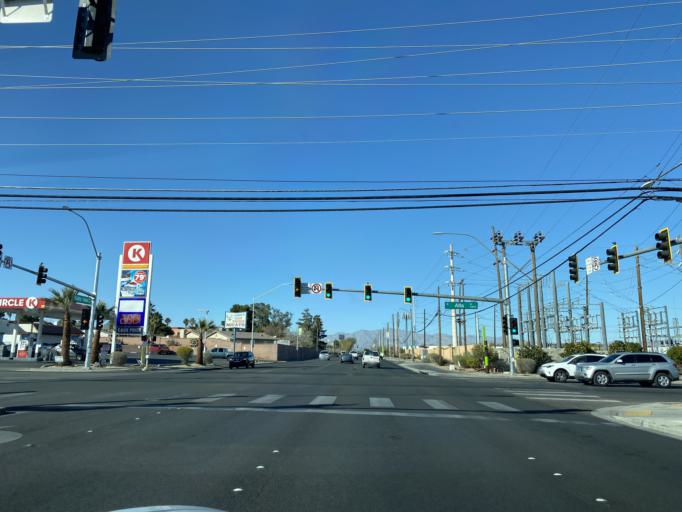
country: US
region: Nevada
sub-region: Clark County
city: Las Vegas
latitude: 36.1658
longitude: -115.1925
